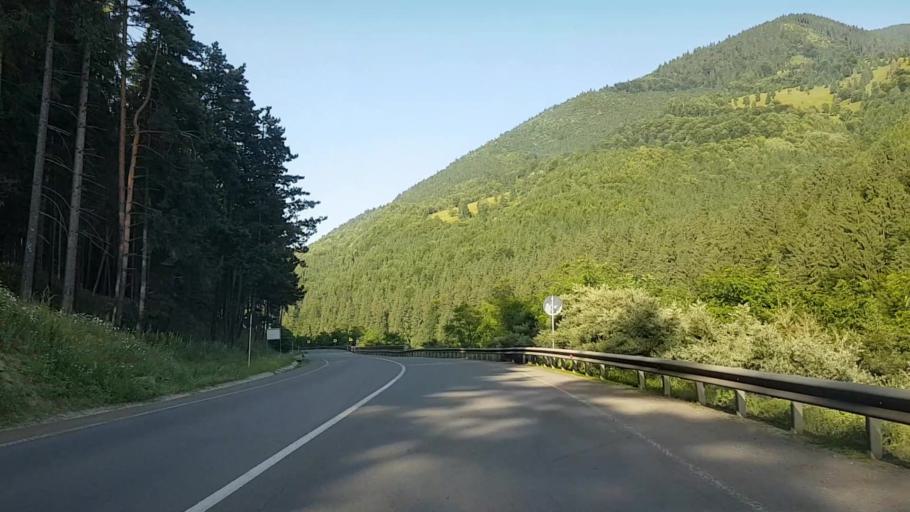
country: RO
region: Bistrita-Nasaud
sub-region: Comuna Tiha Bargaului
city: Tureac
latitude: 47.2105
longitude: 24.8745
